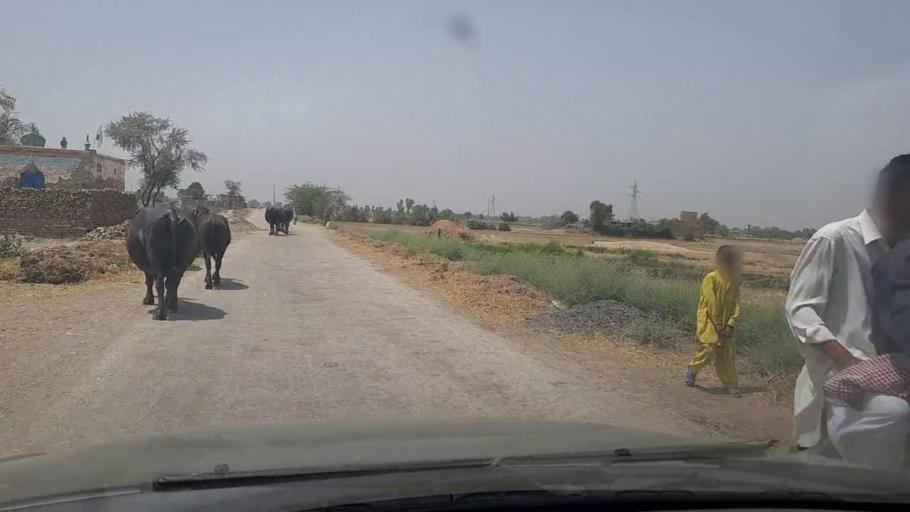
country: PK
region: Sindh
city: Ratodero
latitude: 27.7975
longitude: 68.2594
